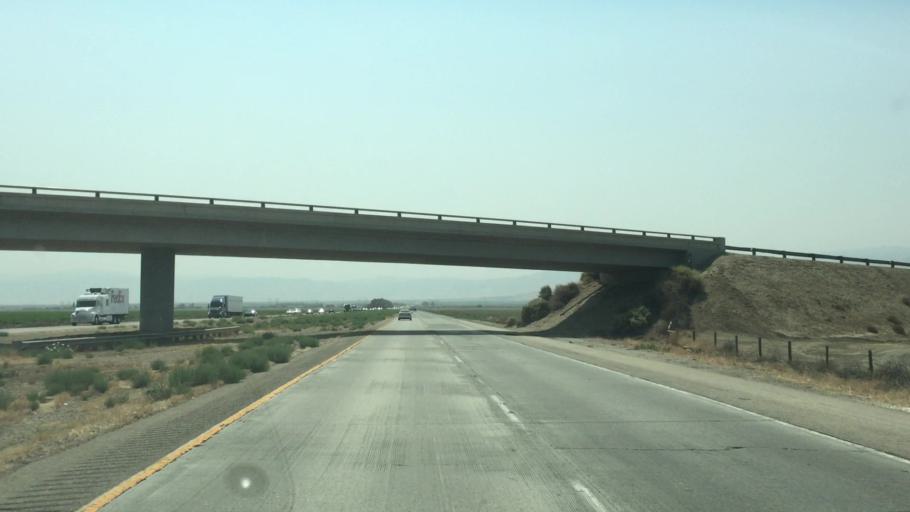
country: US
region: California
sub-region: Kern County
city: Greenfield
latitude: 35.1294
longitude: -119.0754
